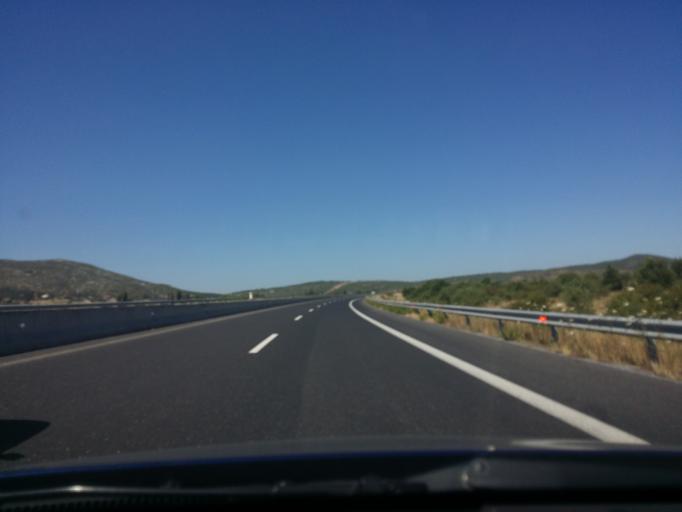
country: GR
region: Peloponnese
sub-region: Nomos Arkadias
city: Megalopoli
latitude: 37.3898
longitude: 22.2432
